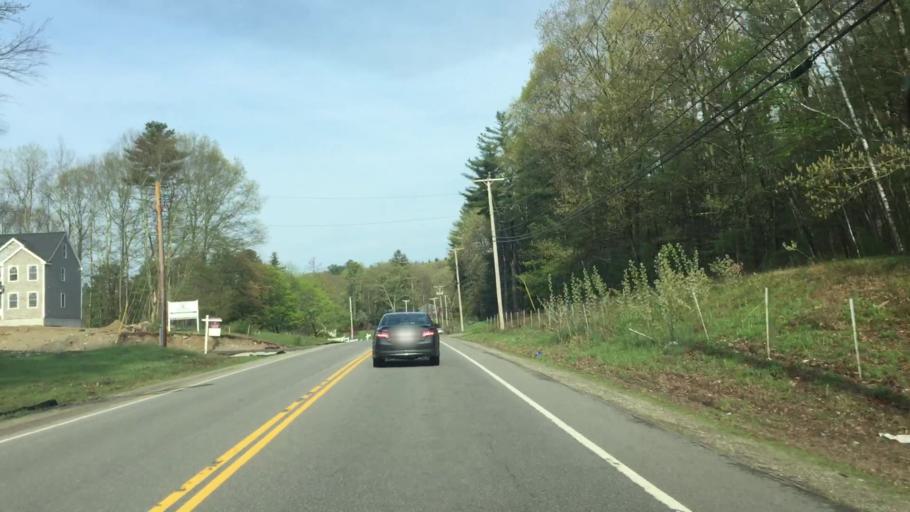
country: US
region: New Hampshire
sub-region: Hillsborough County
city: Pelham
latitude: 42.7040
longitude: -71.3614
